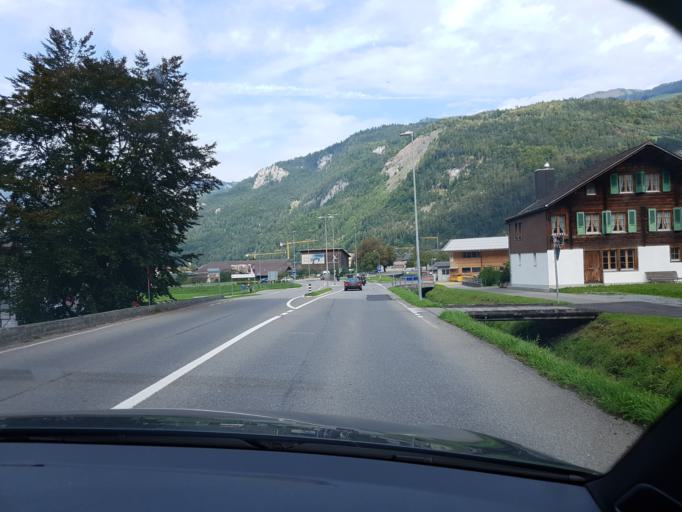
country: CH
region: Bern
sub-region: Interlaken-Oberhasli District
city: Meiringen
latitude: 46.7202
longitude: 8.1900
